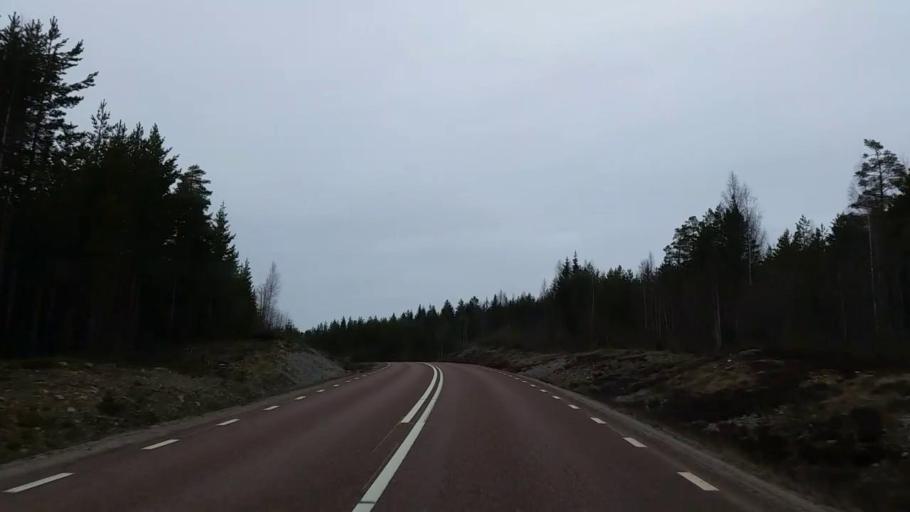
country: SE
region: Gaevleborg
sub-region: Ovanakers Kommun
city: Edsbyn
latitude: 61.2171
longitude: 15.8773
